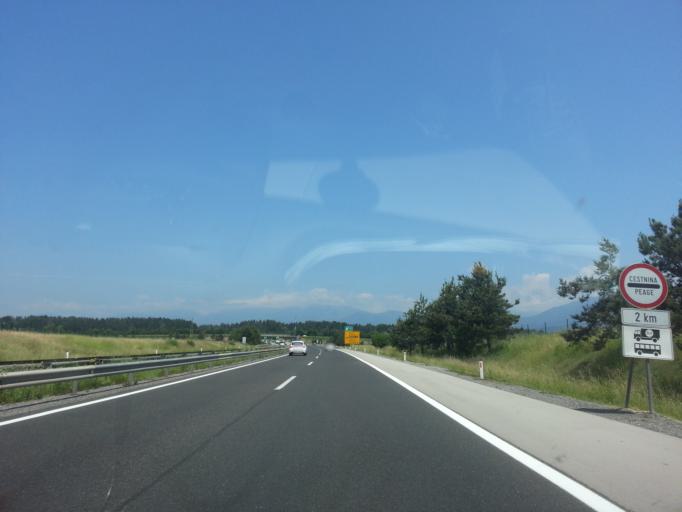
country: SI
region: Vodice
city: Vodice
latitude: 46.1786
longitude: 14.4857
